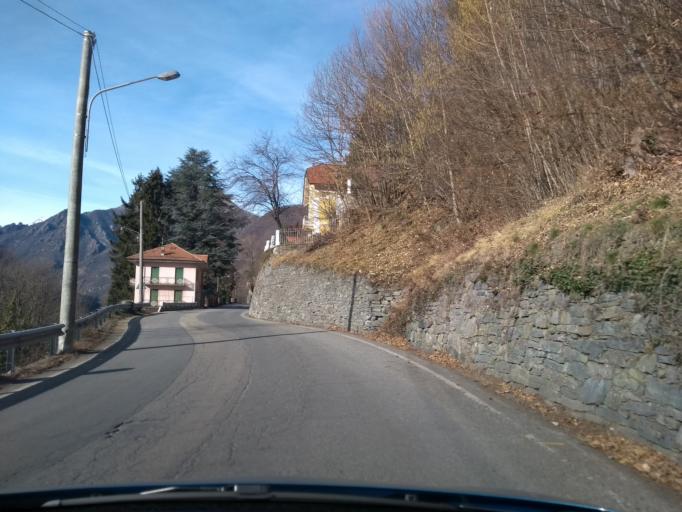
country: IT
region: Piedmont
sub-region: Provincia di Torino
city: Ceres
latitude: 45.3140
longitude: 7.3841
